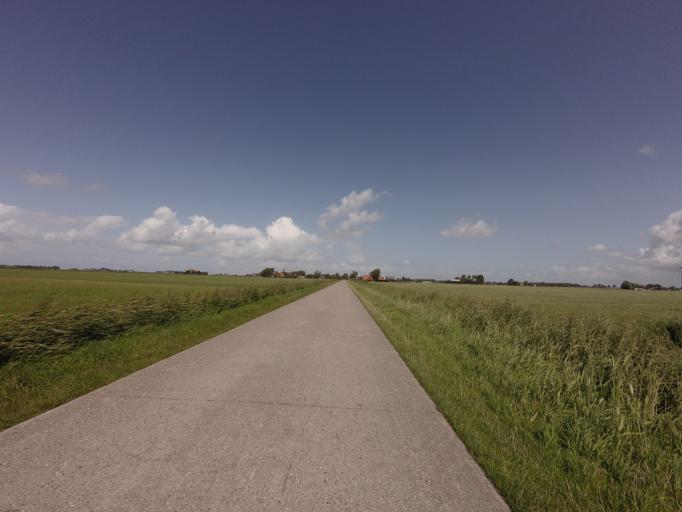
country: NL
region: Friesland
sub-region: Sudwest Fryslan
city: Makkum
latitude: 53.0730
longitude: 5.4536
